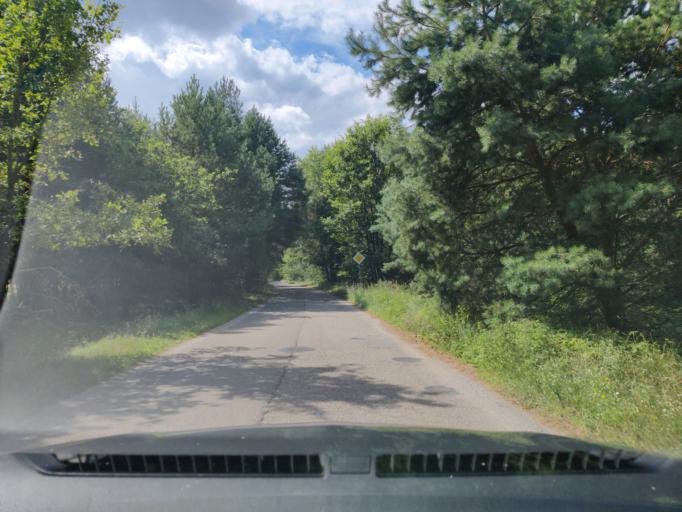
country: PL
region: Masovian Voivodeship
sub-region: Powiat pultuski
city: Pultusk
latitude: 52.7262
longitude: 21.1310
